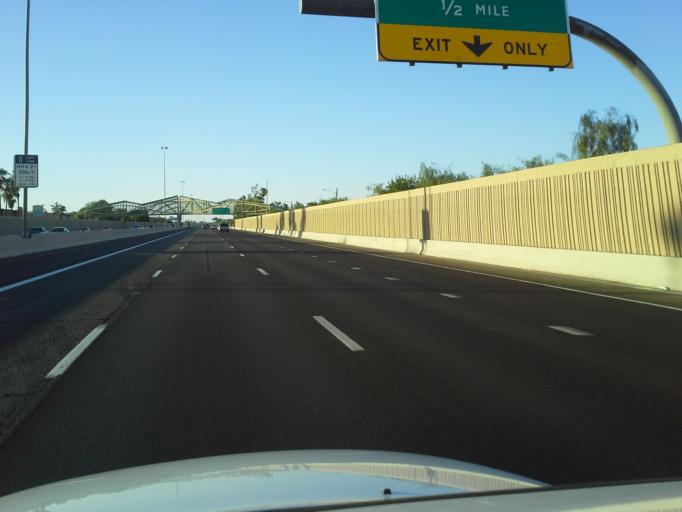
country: US
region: Arizona
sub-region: Maricopa County
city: Glendale
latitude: 33.5288
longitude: -112.1122
